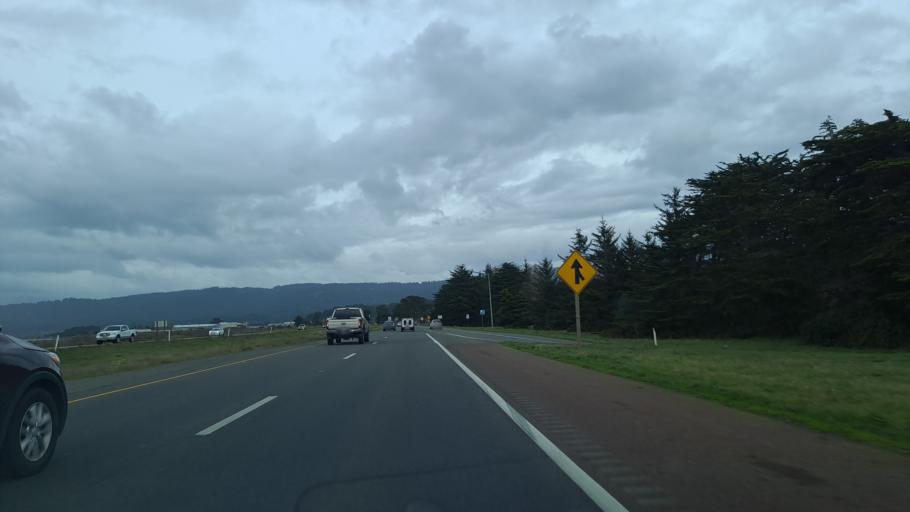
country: US
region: California
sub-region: Humboldt County
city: Bayside
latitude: 40.8204
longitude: -124.0931
